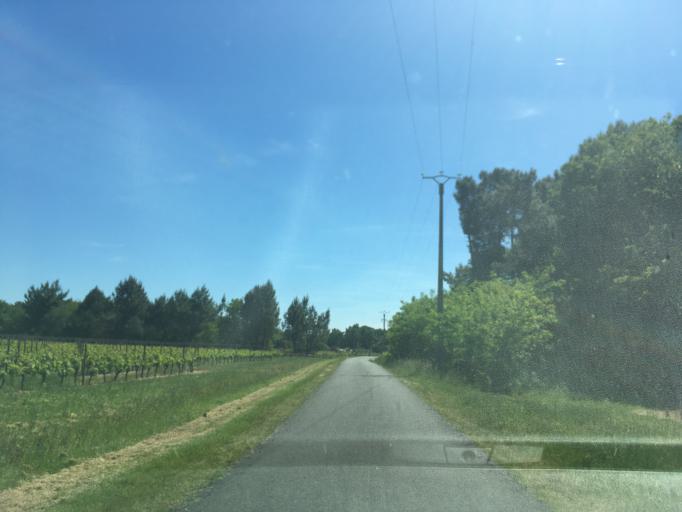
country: FR
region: Aquitaine
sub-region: Departement de la Gironde
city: Lesparre-Medoc
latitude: 45.3000
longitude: -0.8901
